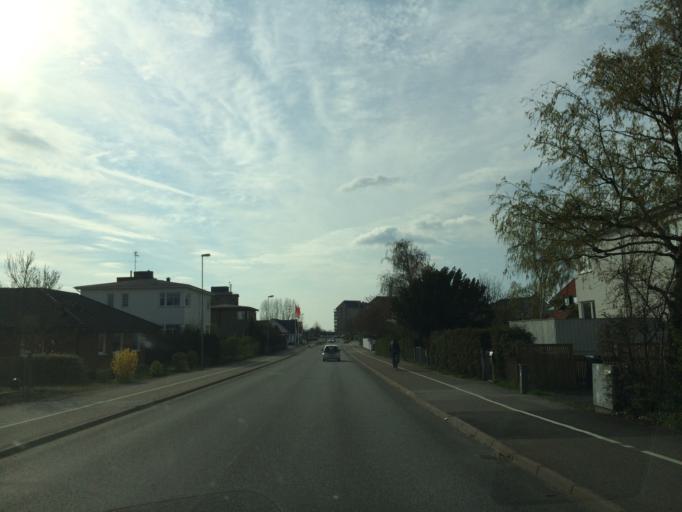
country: SE
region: Skane
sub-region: Lomma Kommun
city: Lomma
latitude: 55.6694
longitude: 13.0716
